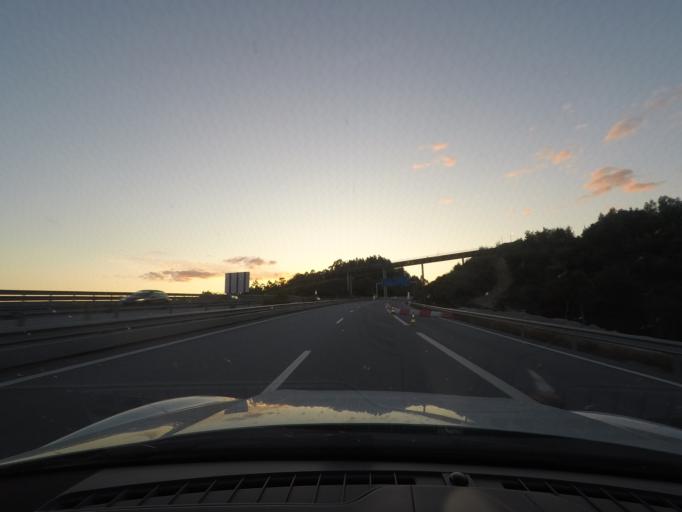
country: PT
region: Braga
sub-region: Guimaraes
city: Serzedo
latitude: 41.3976
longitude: -8.2405
